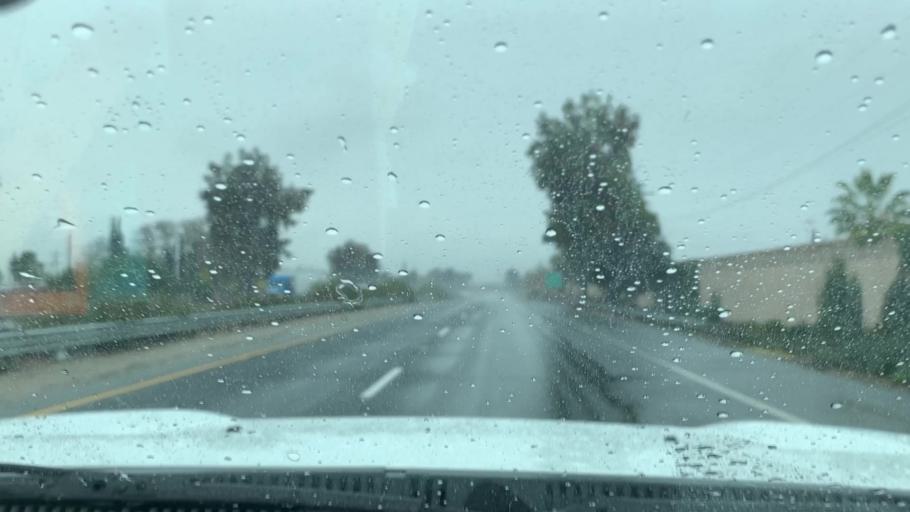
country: US
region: California
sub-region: Tulare County
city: Earlimart
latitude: 35.8810
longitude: -119.2712
